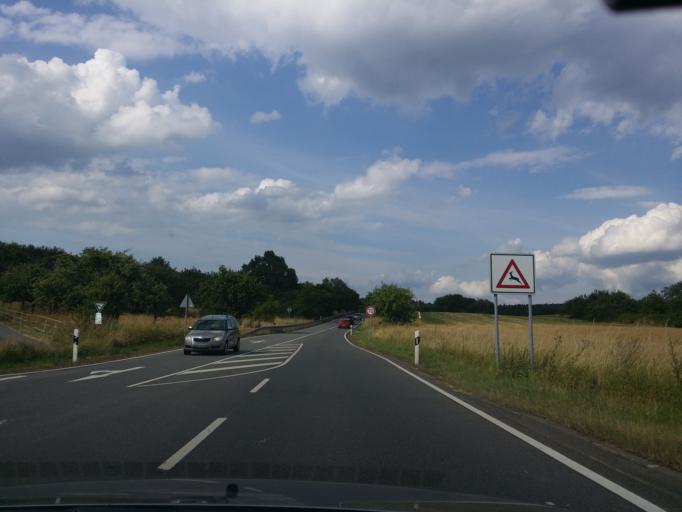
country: DE
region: Hesse
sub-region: Regierungsbezirk Darmstadt
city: Wiesbaden
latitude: 50.1105
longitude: 8.2820
